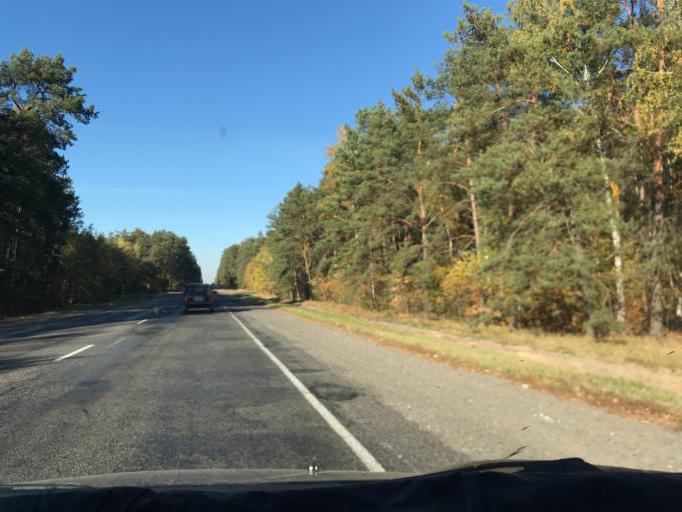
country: BY
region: Gomel
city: Kalinkavichy
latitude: 52.0544
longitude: 29.3611
